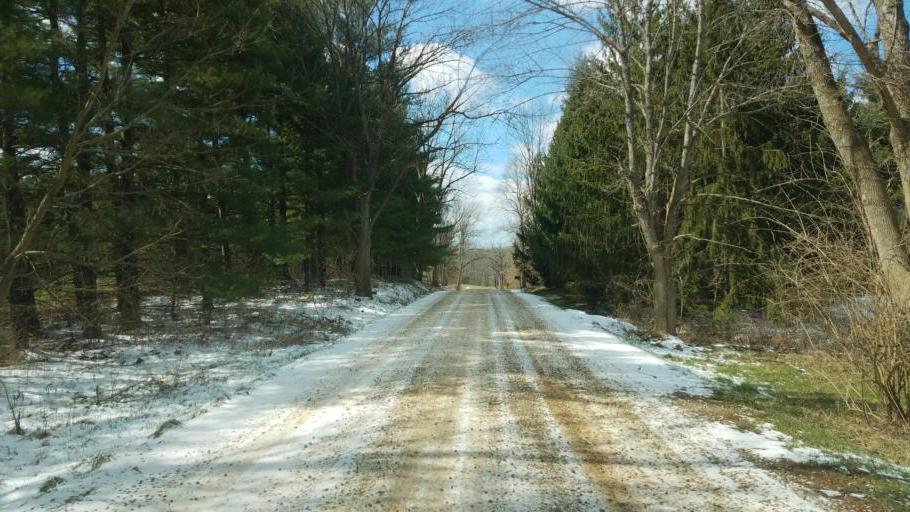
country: US
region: Ohio
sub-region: Knox County
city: Mount Vernon
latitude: 40.3358
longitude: -82.5210
